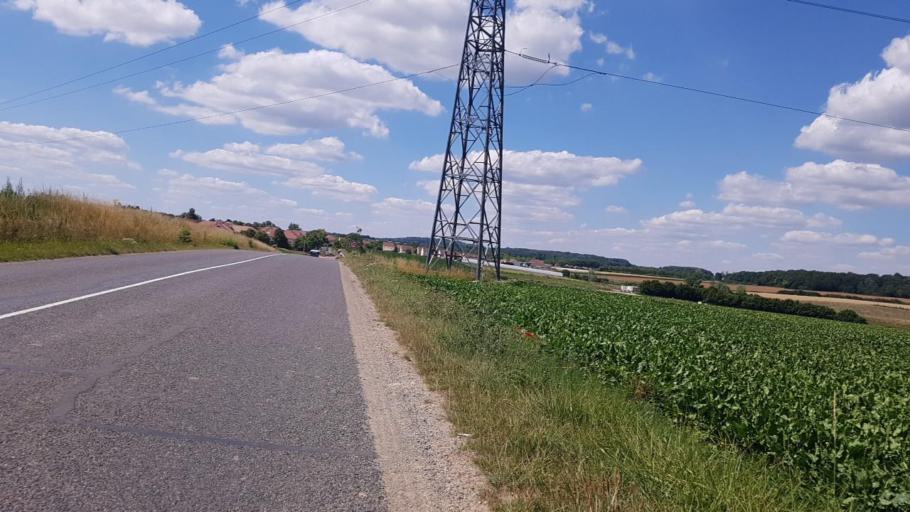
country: FR
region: Ile-de-France
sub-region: Departement de Seine-et-Marne
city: Moussy-le-Neuf
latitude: 49.0570
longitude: 2.6139
